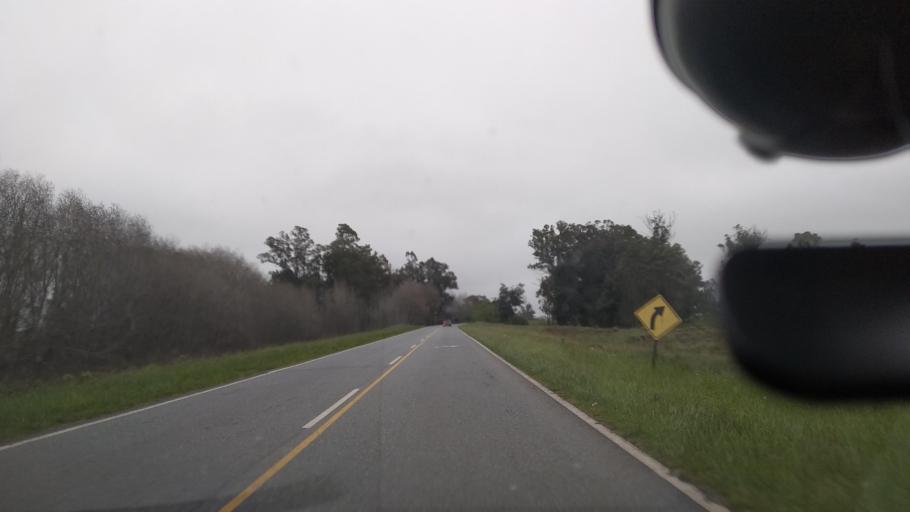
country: AR
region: Buenos Aires
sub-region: Partido de Magdalena
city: Magdalena
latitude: -35.2652
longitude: -57.6238
